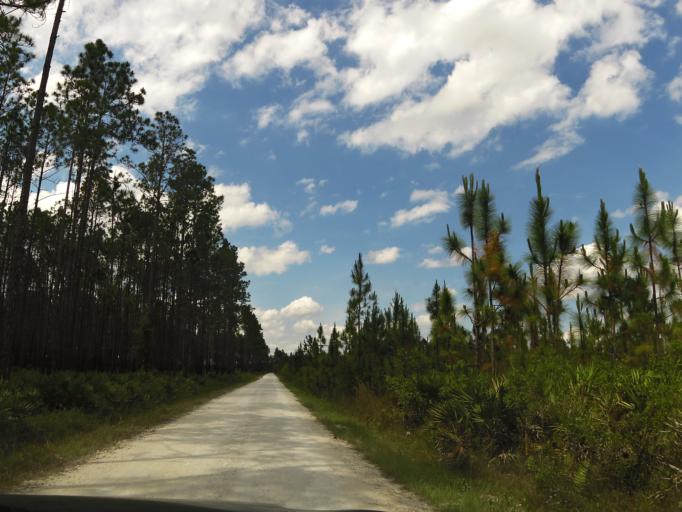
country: US
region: Florida
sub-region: Clay County
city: Asbury Lake
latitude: 29.8932
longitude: -81.8500
